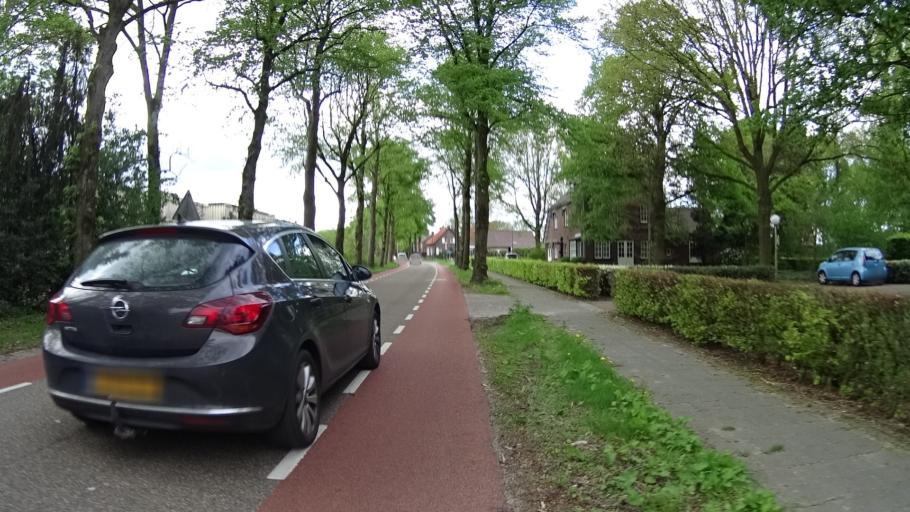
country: NL
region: North Brabant
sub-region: Gemeente Boekel
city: Boekel
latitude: 51.5881
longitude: 5.7077
